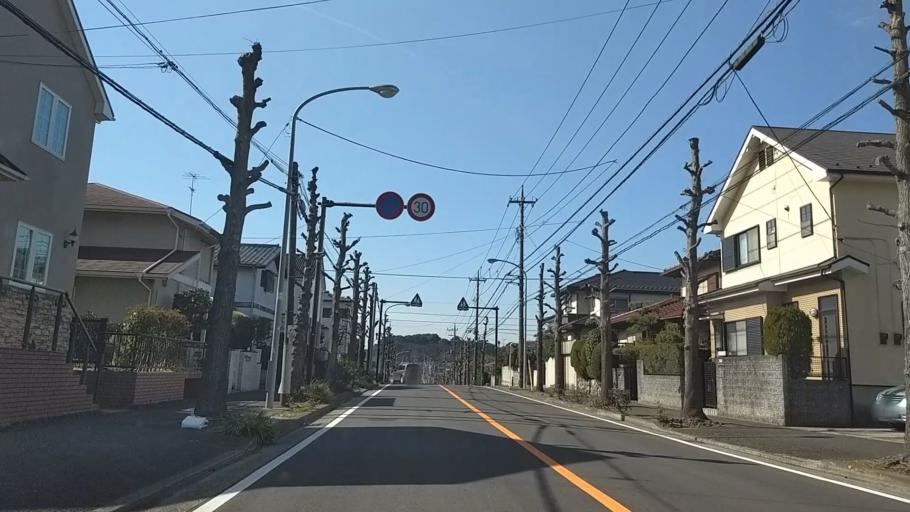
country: JP
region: Kanagawa
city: Kamakura
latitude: 35.3740
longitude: 139.5477
